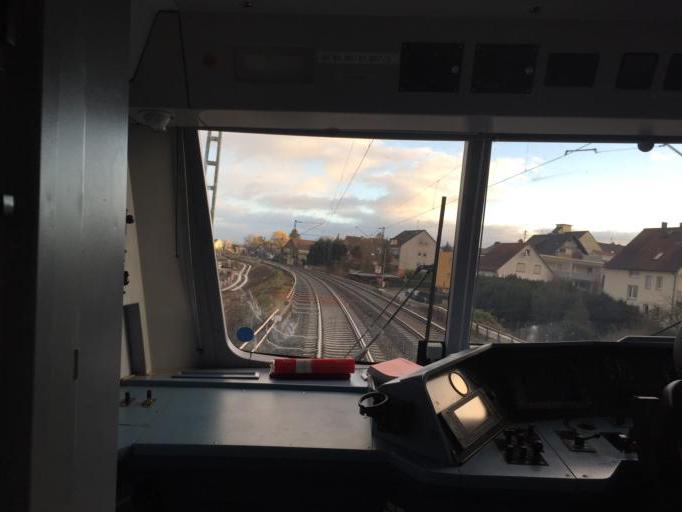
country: DE
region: Hesse
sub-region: Regierungsbezirk Darmstadt
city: Bad Vilbel
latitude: 50.1724
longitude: 8.6932
